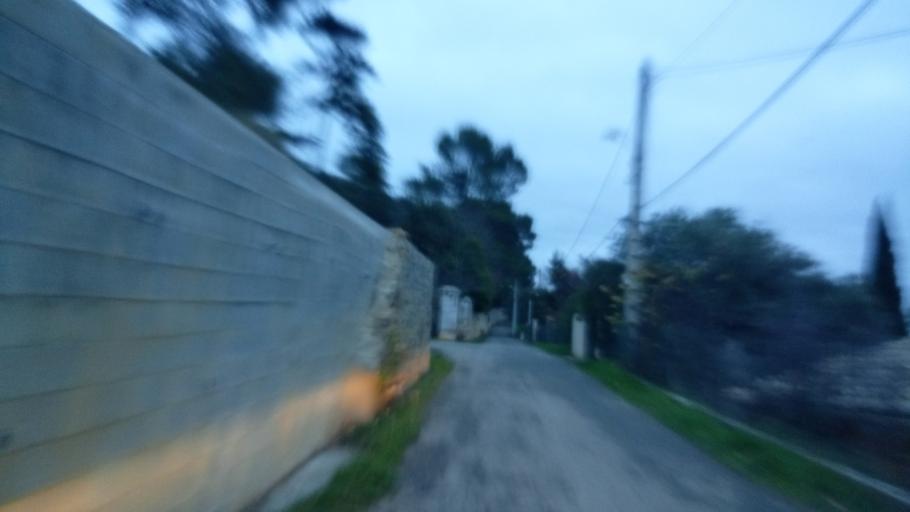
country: FR
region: Provence-Alpes-Cote d'Azur
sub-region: Departement du Var
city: Saint-Julien
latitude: 43.6366
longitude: 5.9373
